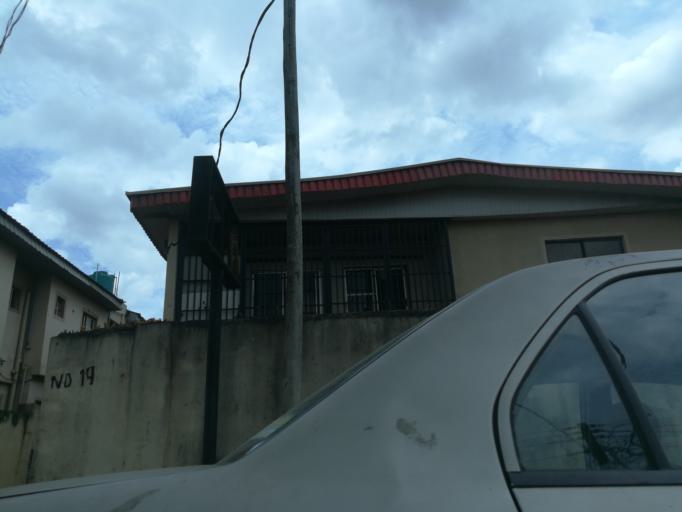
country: NG
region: Lagos
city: Ikeja
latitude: 6.5976
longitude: 3.3484
